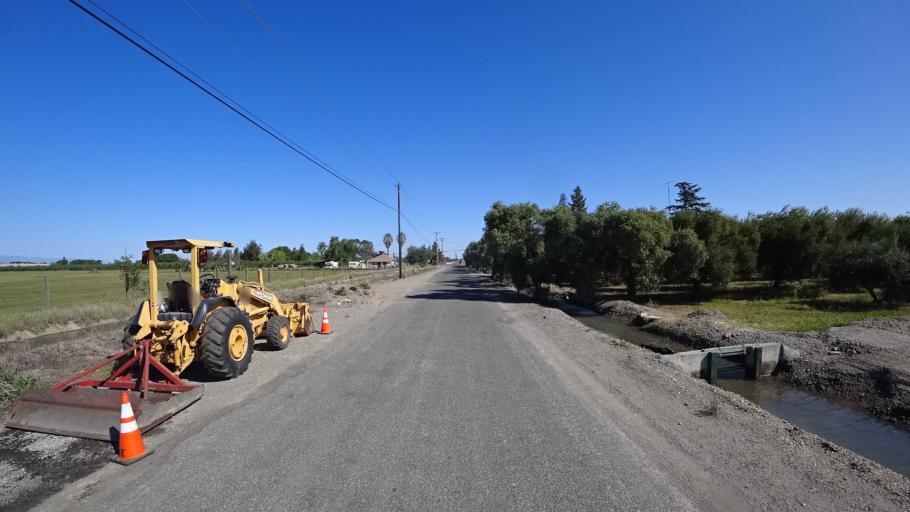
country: US
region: California
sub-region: Glenn County
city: Orland
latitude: 39.7347
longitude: -122.1688
